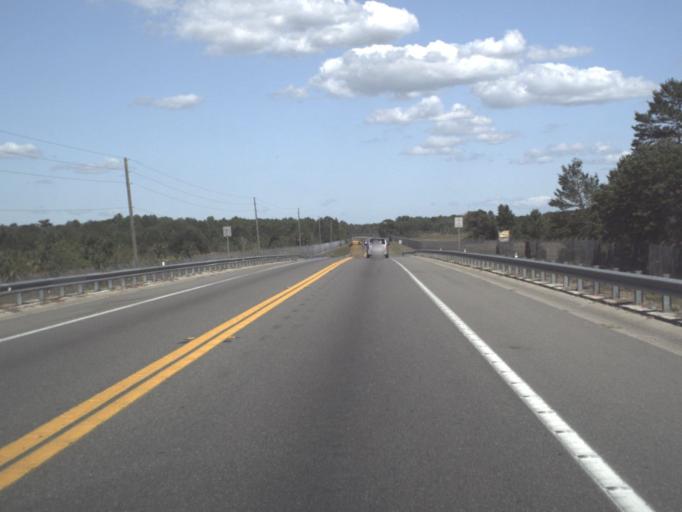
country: US
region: Florida
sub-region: Lake County
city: Mount Plymouth
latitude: 28.8110
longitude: -81.4546
